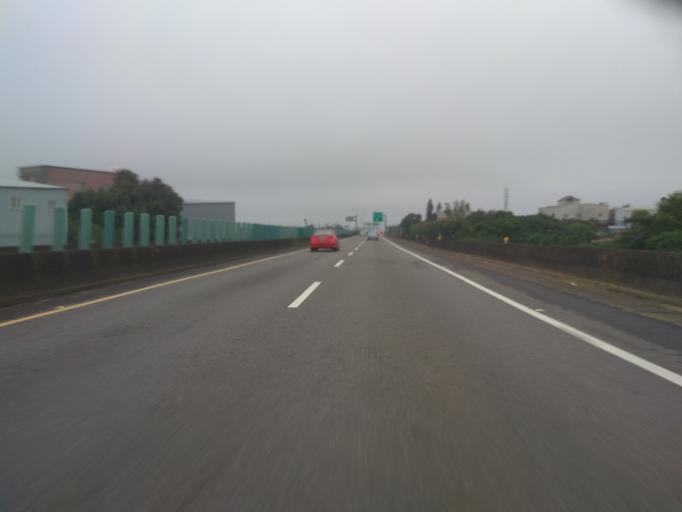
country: TW
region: Taiwan
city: Taoyuan City
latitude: 24.9854
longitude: 121.1269
